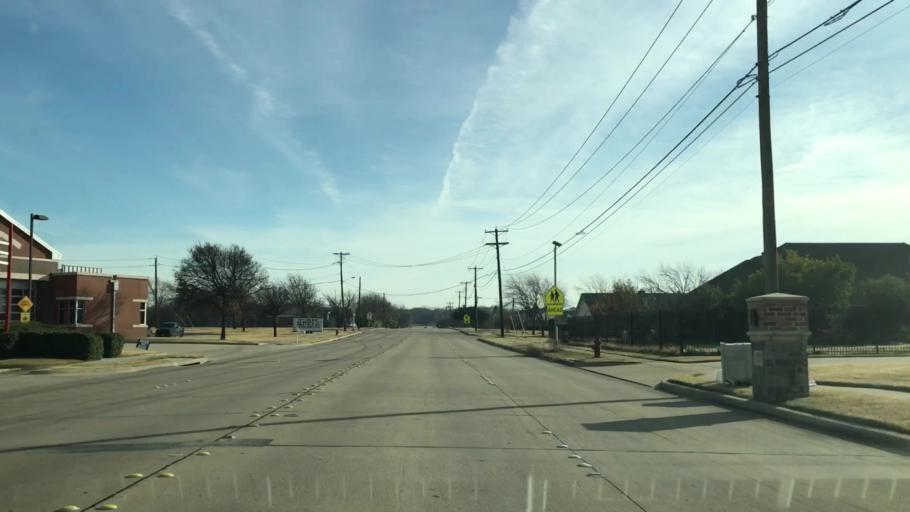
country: US
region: Texas
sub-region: Tarrant County
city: Watauga
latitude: 32.8749
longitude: -97.2264
